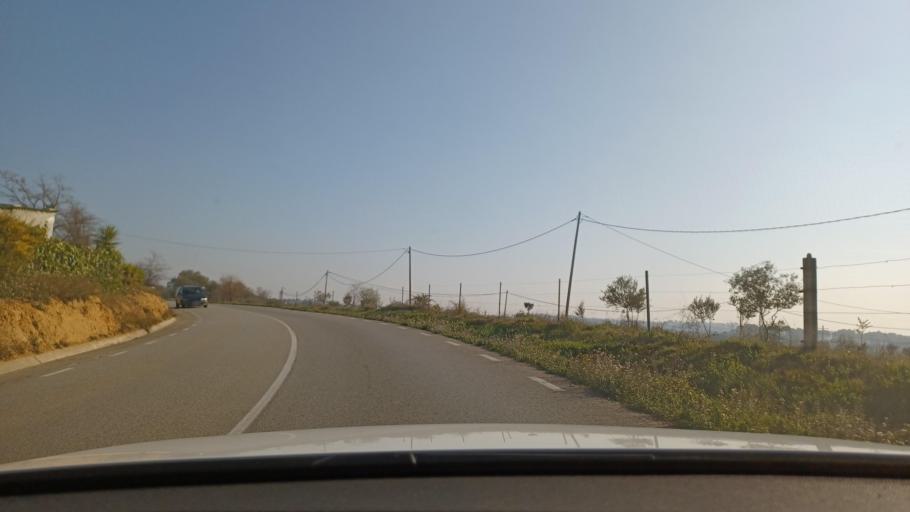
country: ES
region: Catalonia
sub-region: Provincia de Barcelona
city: Santa Eulalia de Roncana
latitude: 41.6608
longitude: 2.2402
